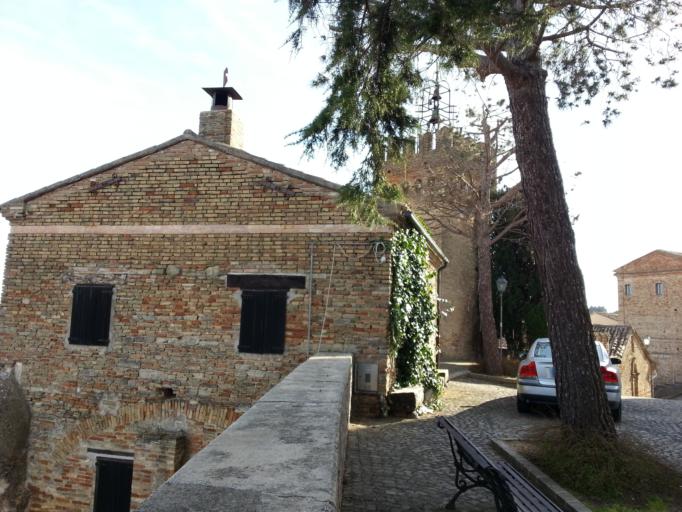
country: IT
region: The Marches
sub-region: Provincia di Ancona
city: Offagna
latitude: 43.5277
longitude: 13.4418
